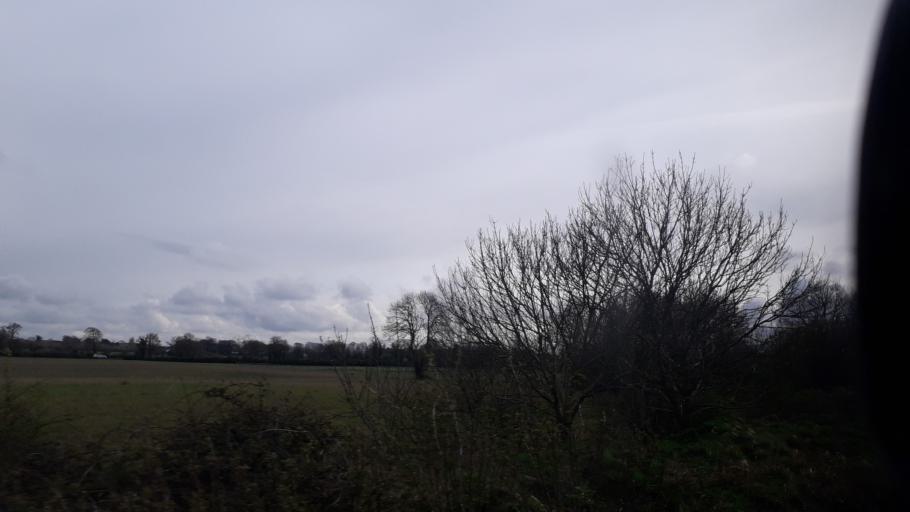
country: IE
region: Leinster
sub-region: An Mhi
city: Enfield
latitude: 53.4189
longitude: -6.7868
